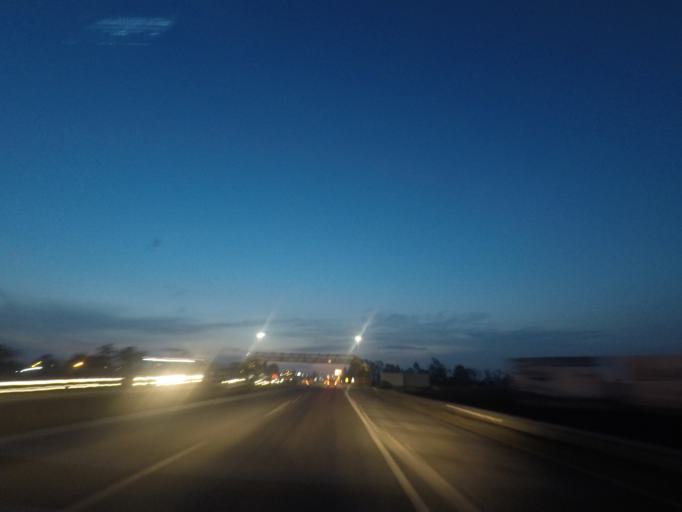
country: BR
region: Parana
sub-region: Sao Jose Dos Pinhais
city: Sao Jose dos Pinhais
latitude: -25.4943
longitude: -49.1669
